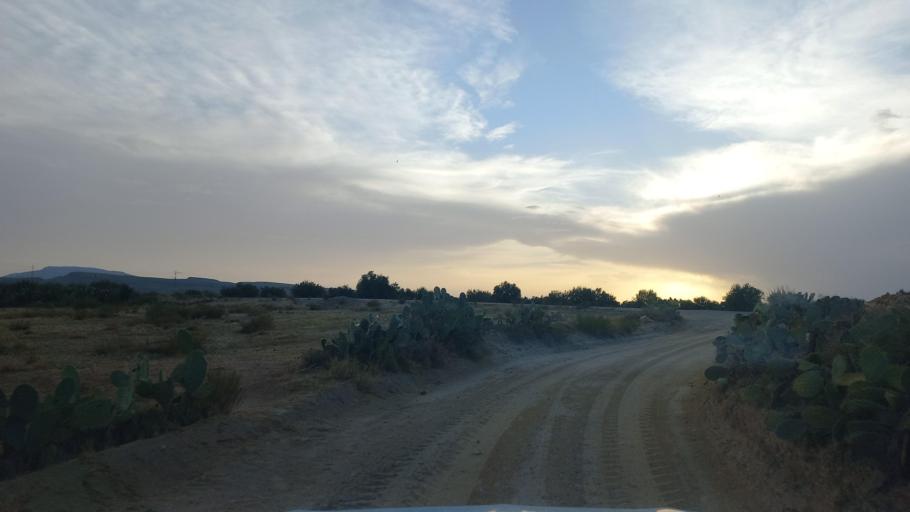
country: TN
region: Al Qasrayn
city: Kasserine
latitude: 35.2119
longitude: 9.0428
